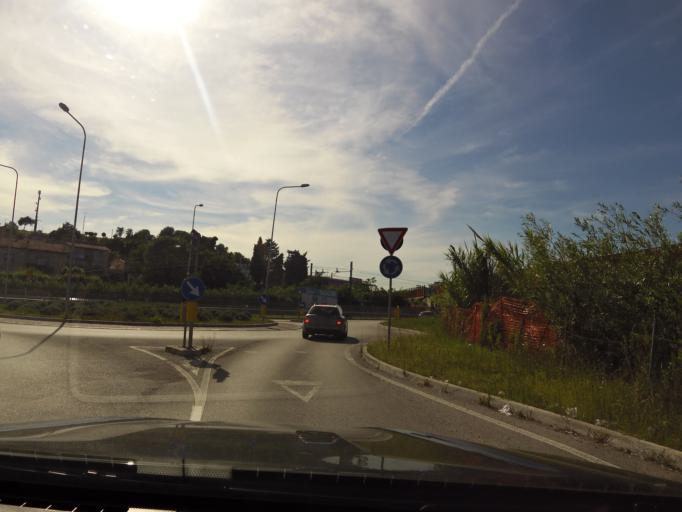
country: IT
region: The Marches
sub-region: Provincia di Ancona
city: San Biagio
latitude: 43.5250
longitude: 13.5231
